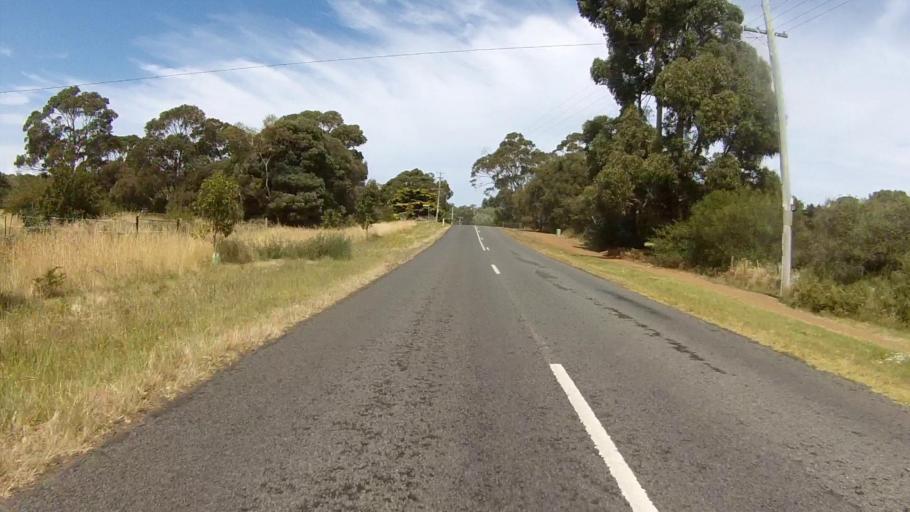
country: AU
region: Tasmania
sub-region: Kingborough
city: Taroona
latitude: -43.0116
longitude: 147.4132
